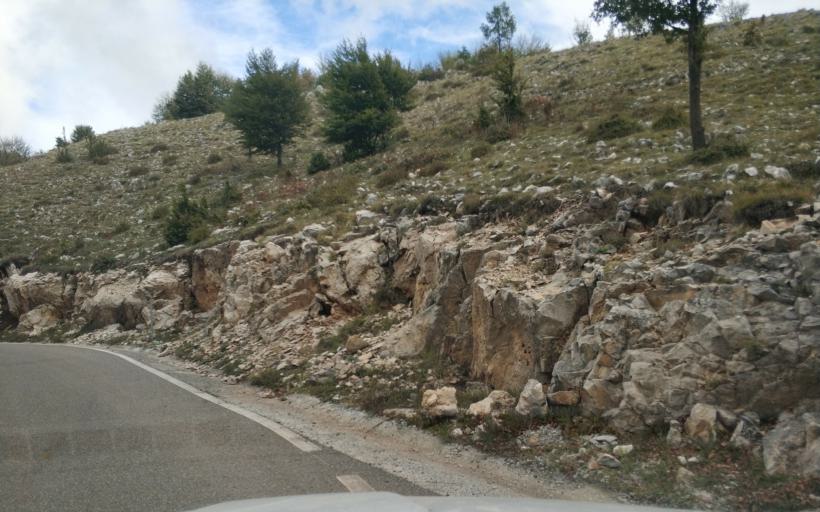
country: AL
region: Durres
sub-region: Rrethi i Krujes
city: Kruje
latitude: 41.5179
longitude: 19.8081
